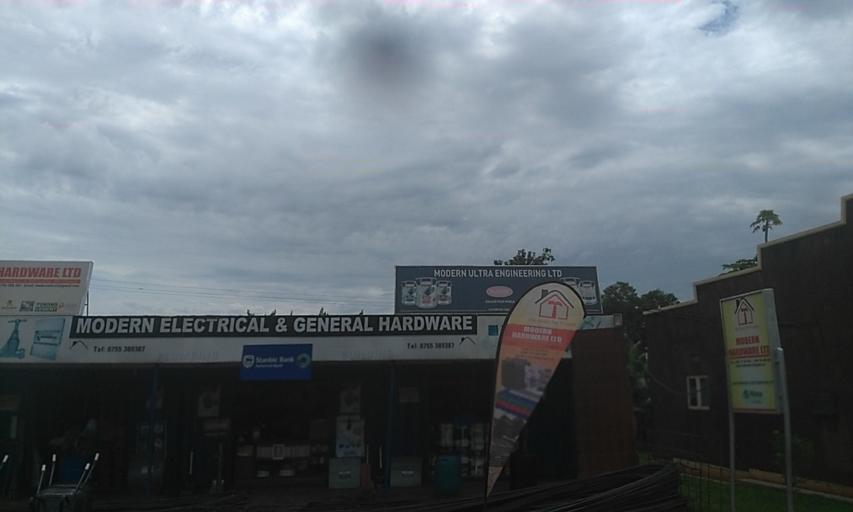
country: UG
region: Central Region
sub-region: Wakiso District
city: Bweyogerere
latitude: 0.3957
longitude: 32.6957
